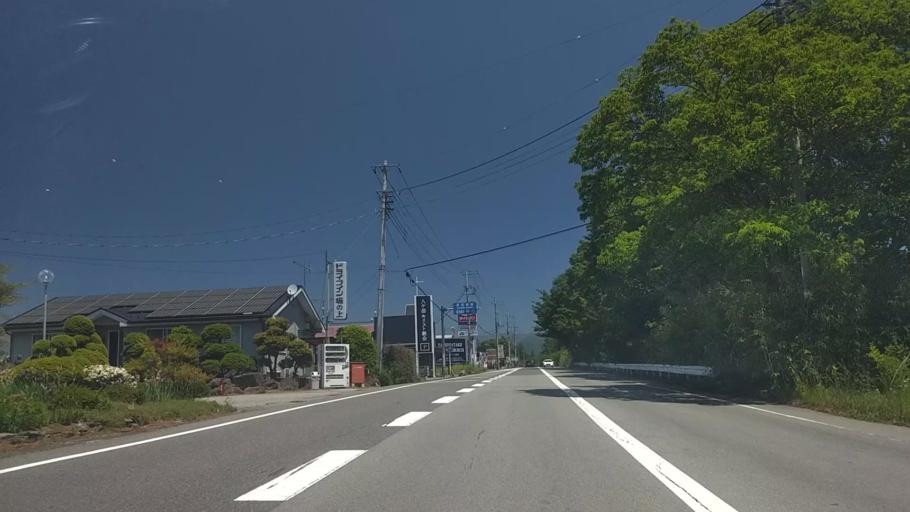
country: JP
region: Yamanashi
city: Nirasaki
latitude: 35.8083
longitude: 138.4281
